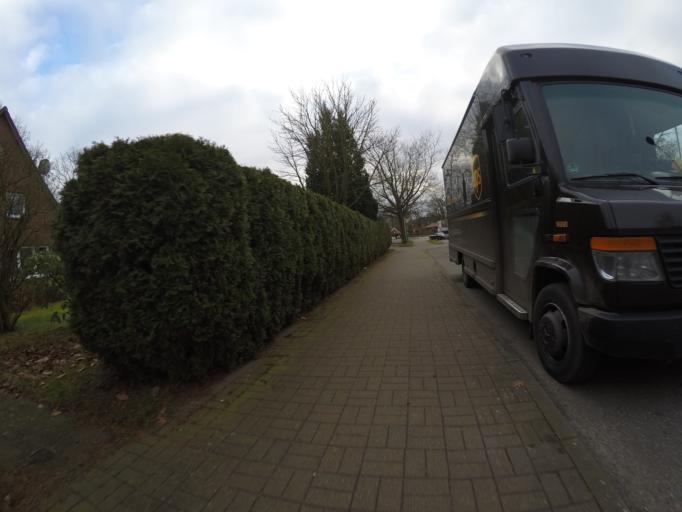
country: DE
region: Schleswig-Holstein
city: Alveslohe
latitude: 53.7909
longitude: 9.9155
